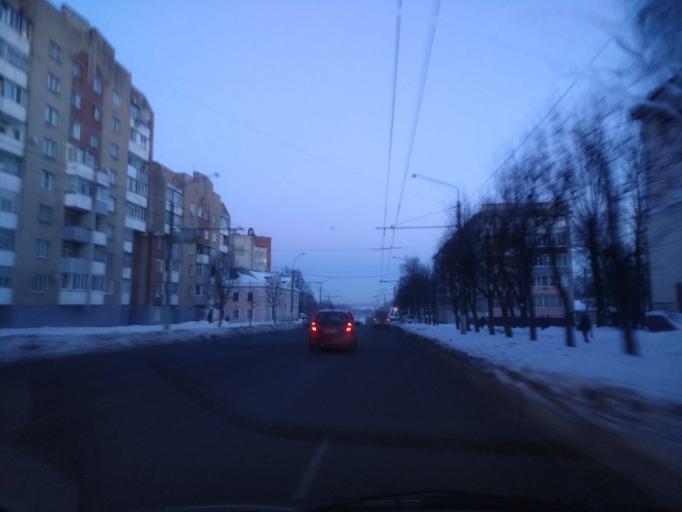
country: BY
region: Mogilev
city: Mahilyow
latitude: 53.8937
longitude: 30.3145
